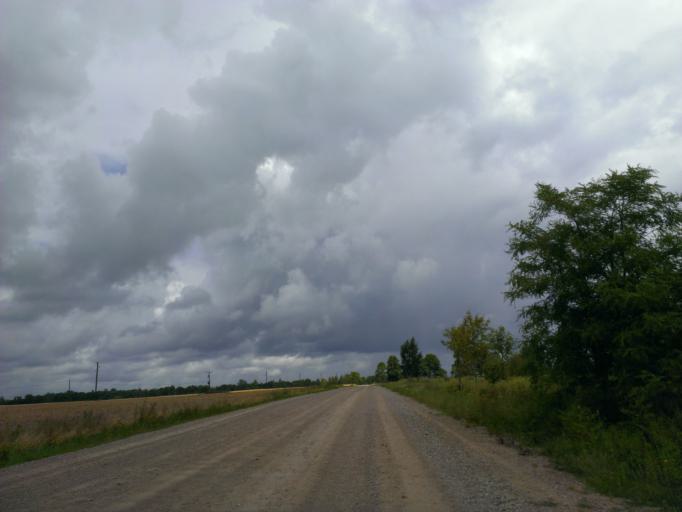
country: LV
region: Sigulda
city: Sigulda
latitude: 57.1909
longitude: 24.9419
